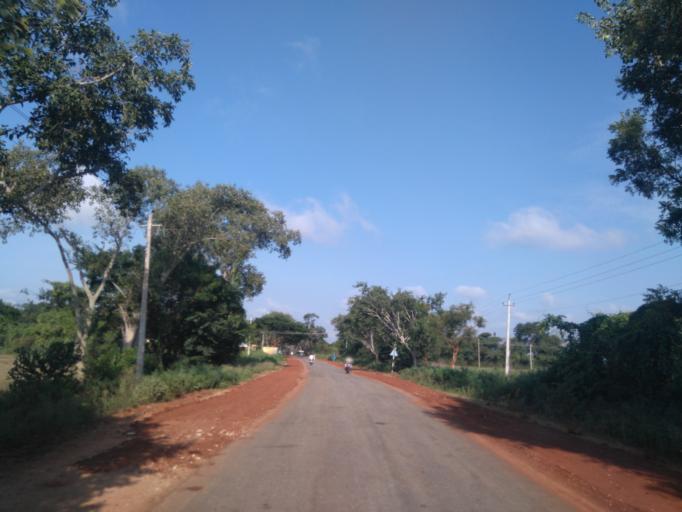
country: IN
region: Karnataka
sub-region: Mandya
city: Malavalli
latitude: 12.2659
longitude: 77.0276
